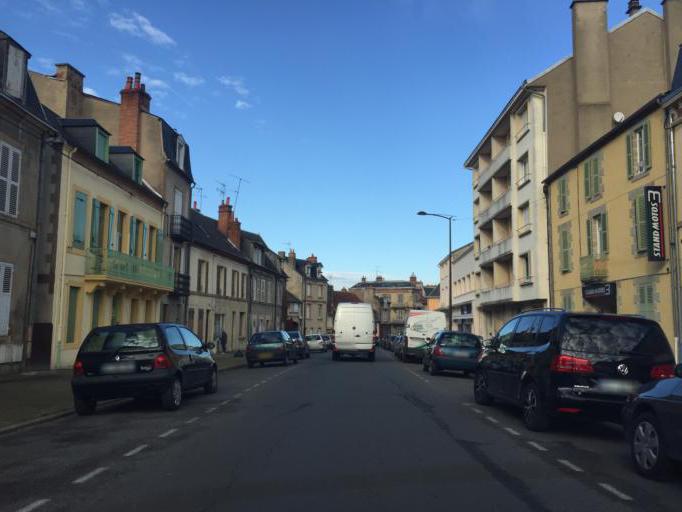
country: FR
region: Auvergne
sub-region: Departement de l'Allier
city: Moulins
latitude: 46.5590
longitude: 3.3338
